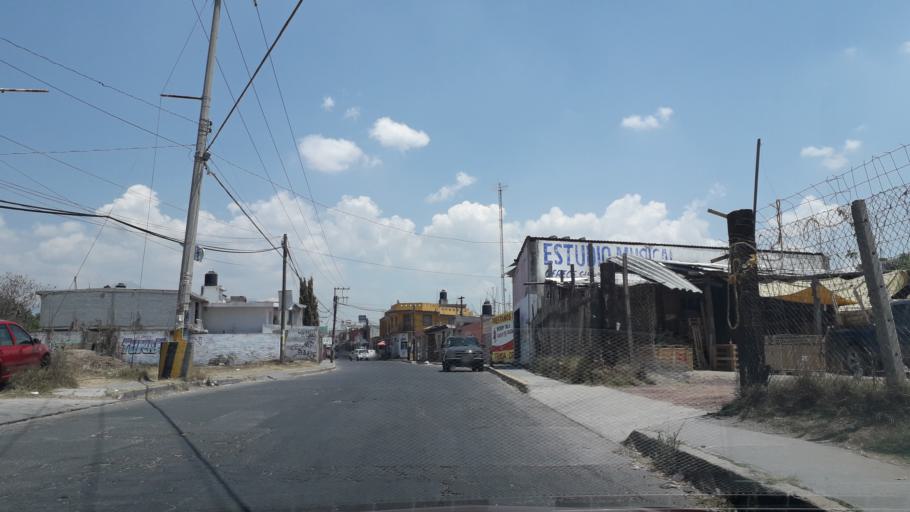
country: MX
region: Puebla
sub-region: Puebla
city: Santa Maria Xonacatepec
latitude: 19.0830
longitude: -98.1075
